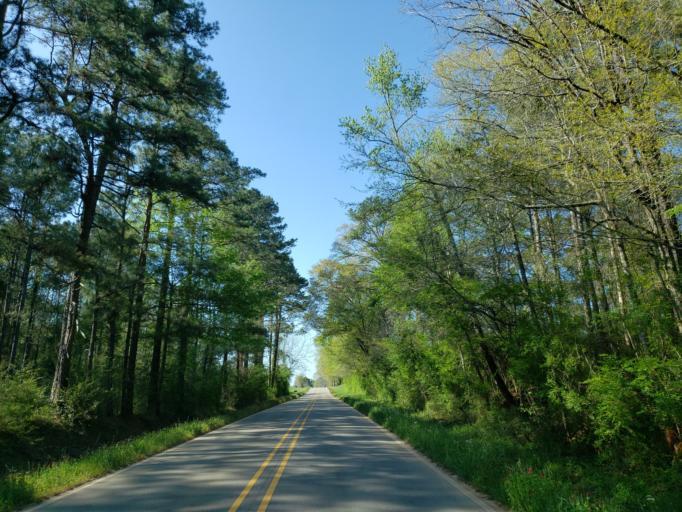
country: US
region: Mississippi
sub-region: Covington County
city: Collins
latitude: 31.6043
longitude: -89.3793
